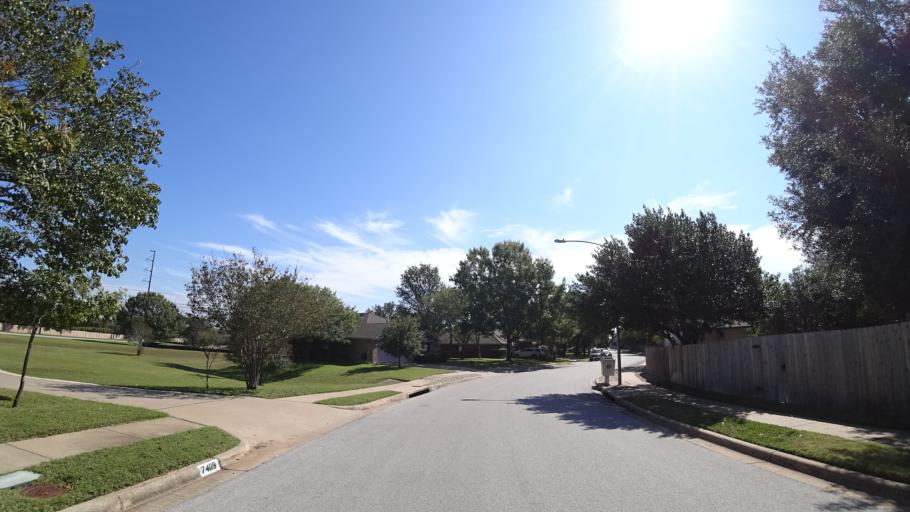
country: US
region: Texas
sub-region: Travis County
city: Shady Hollow
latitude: 30.2195
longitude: -97.8571
